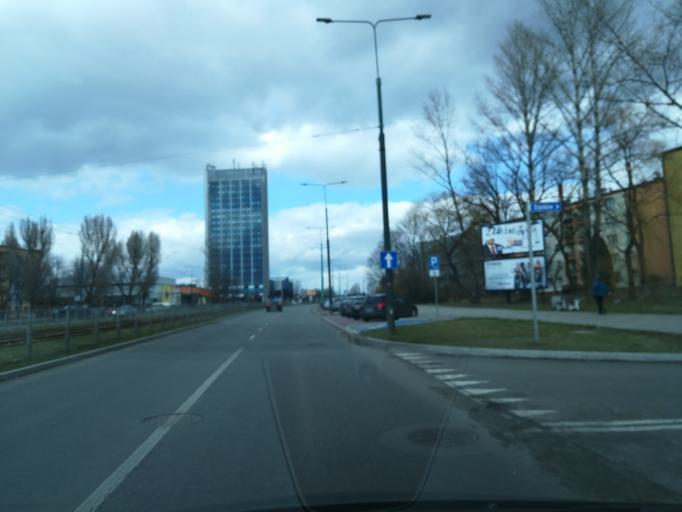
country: PL
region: Silesian Voivodeship
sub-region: Powiat bedzinski
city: Bedzin
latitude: 50.2960
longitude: 19.1340
